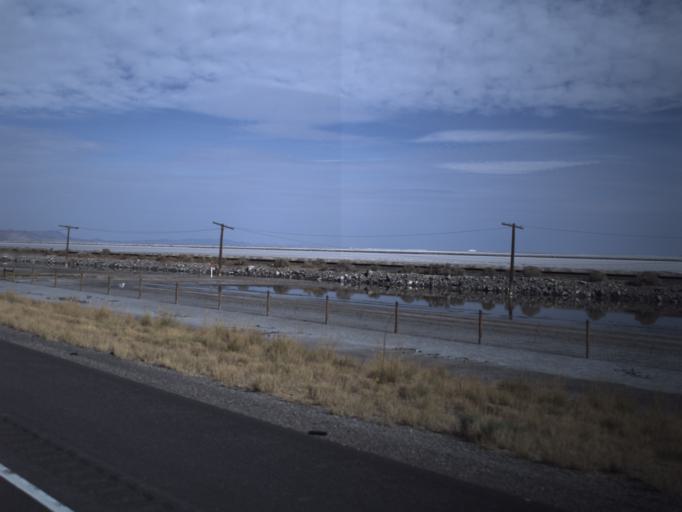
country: US
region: Utah
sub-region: Tooele County
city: Grantsville
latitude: 40.7198
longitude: -112.5530
